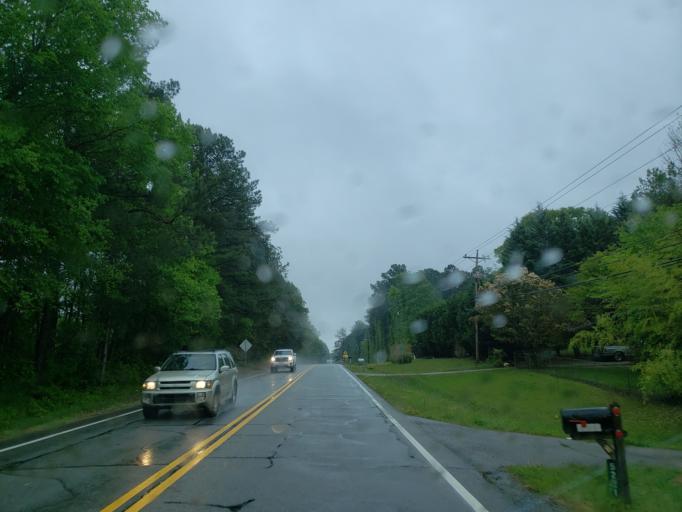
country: US
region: Georgia
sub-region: Paulding County
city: Dallas
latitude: 33.8430
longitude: -84.8621
